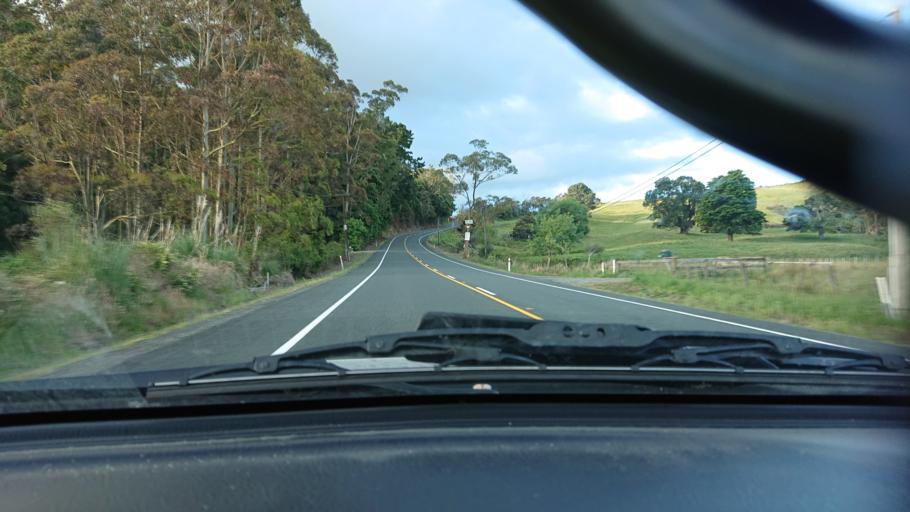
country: NZ
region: Auckland
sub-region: Auckland
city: Parakai
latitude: -36.5285
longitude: 174.4544
